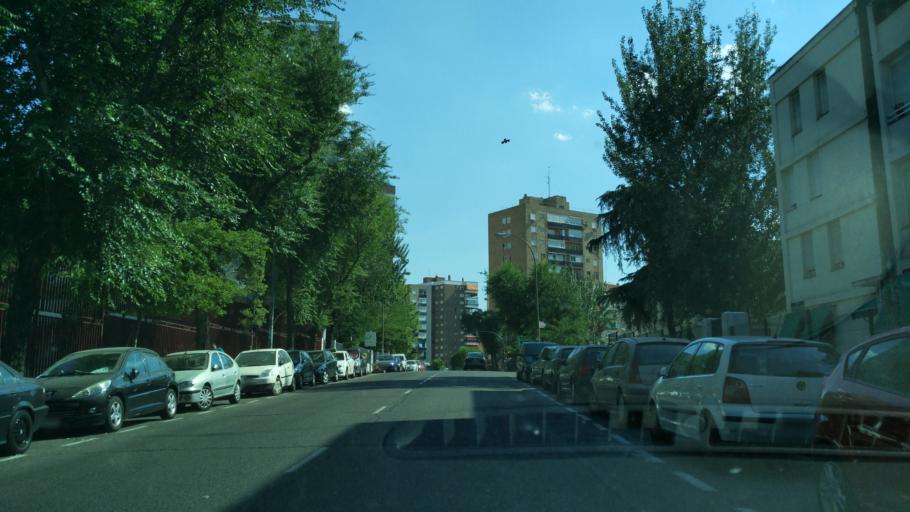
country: ES
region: Madrid
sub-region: Provincia de Madrid
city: Tetuan de las Victorias
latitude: 40.4591
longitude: -3.7126
